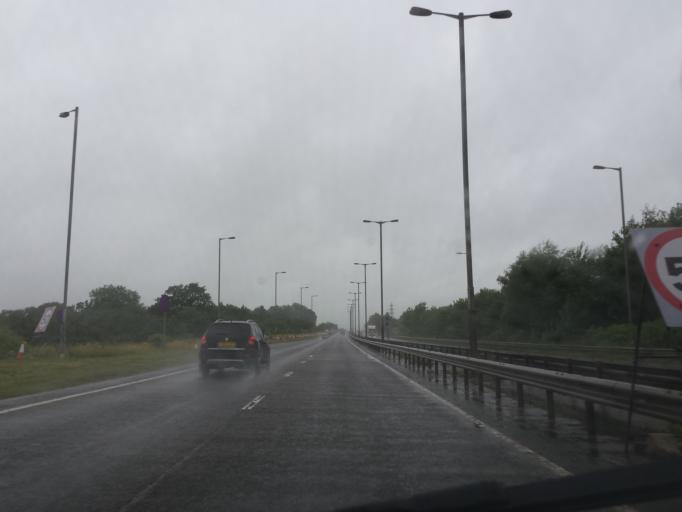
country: GB
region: England
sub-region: Warwickshire
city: Ryton on Dunsmore
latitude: 52.3890
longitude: -1.4402
